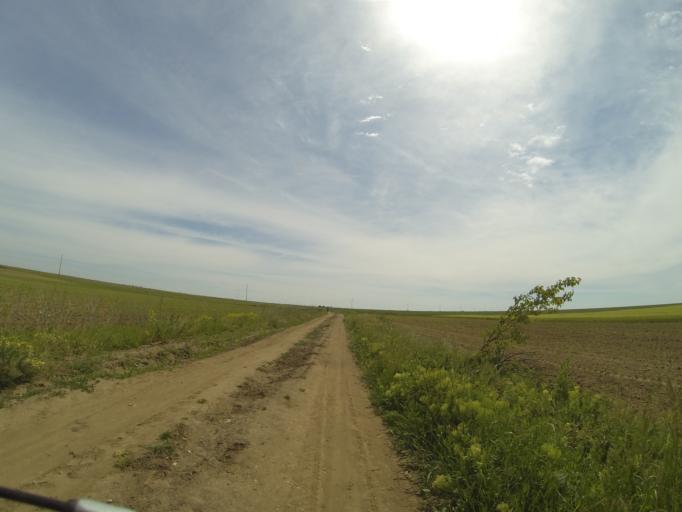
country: RO
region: Dolj
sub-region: Comuna Ghindeni
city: Ghindeni
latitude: 44.2073
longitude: 23.9426
